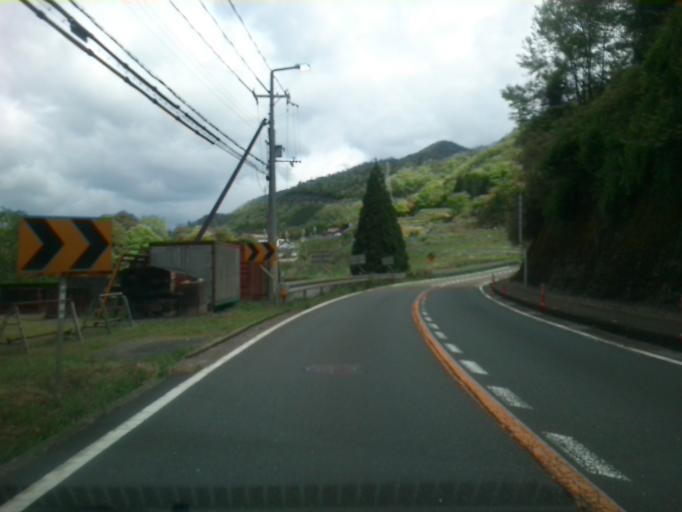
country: JP
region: Kyoto
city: Ayabe
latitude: 35.2196
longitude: 135.4199
